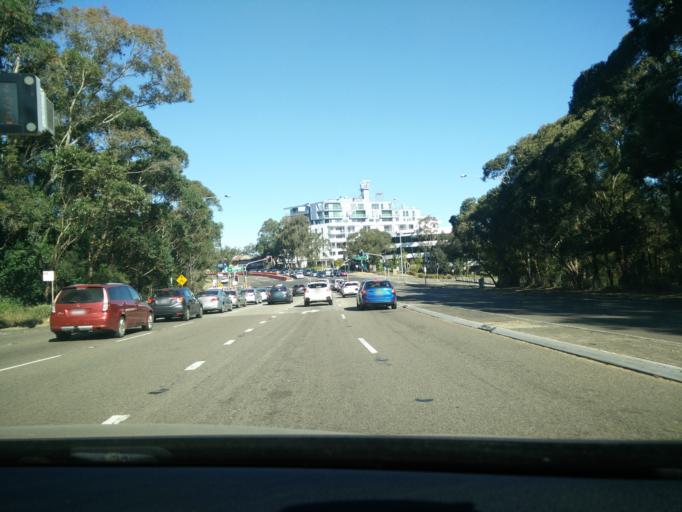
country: AU
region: New South Wales
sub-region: City of Sydney
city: Pymble
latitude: -33.7500
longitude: 151.1467
